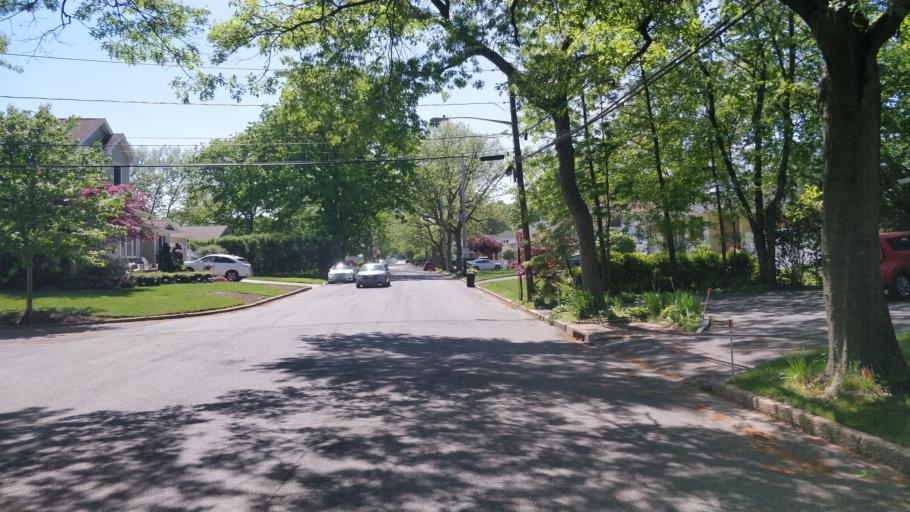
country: US
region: New York
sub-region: Suffolk County
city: Commack
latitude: 40.8464
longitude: -73.3010
